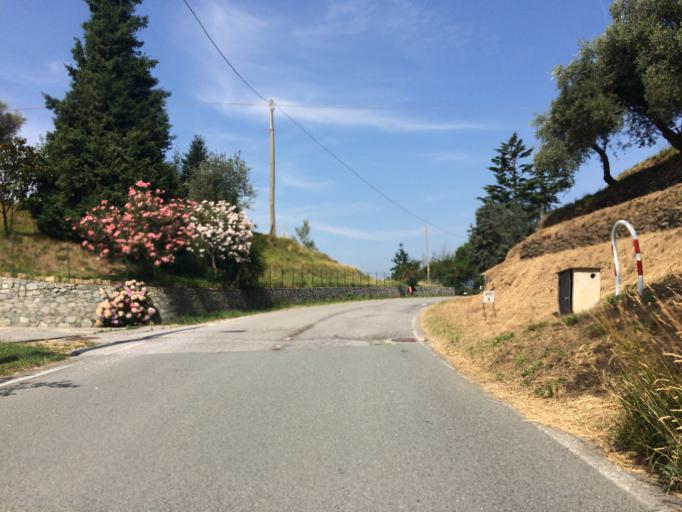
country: IT
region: Liguria
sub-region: Provincia di Savona
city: Varazze
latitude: 44.3846
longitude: 8.5694
